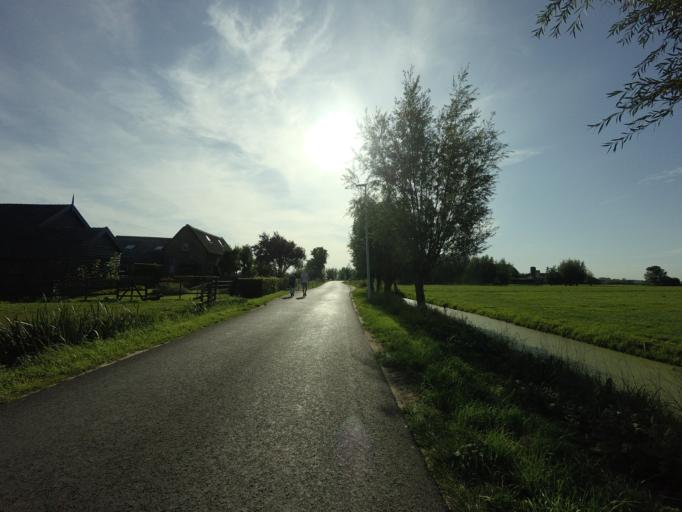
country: NL
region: Utrecht
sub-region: Gemeente Lopik
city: Lopik
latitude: 51.9329
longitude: 4.9837
